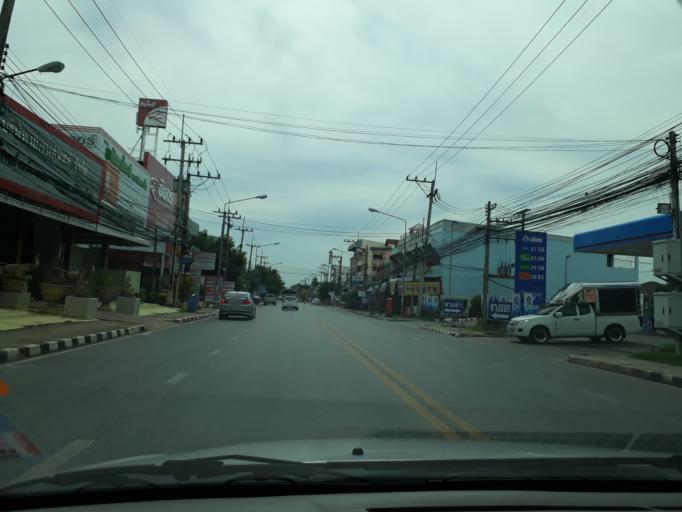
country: TH
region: Khon Kaen
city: Khon Kaen
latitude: 16.4360
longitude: 102.8511
